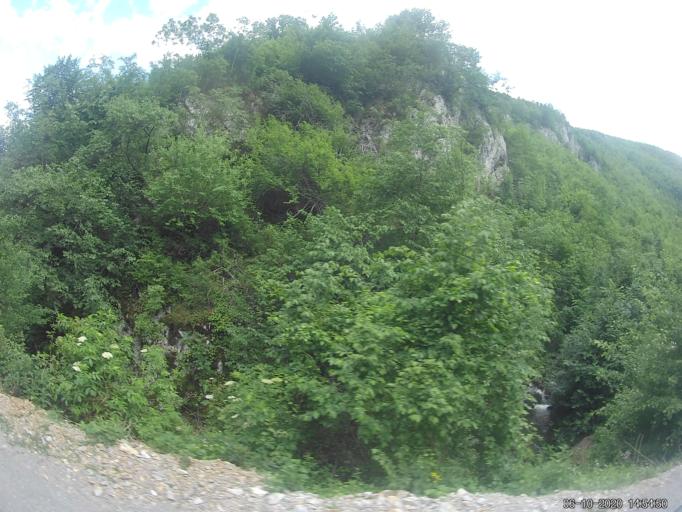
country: XK
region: Ferizaj
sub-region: Komuna e Shtimes
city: Shtime
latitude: 42.4069
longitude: 20.9936
